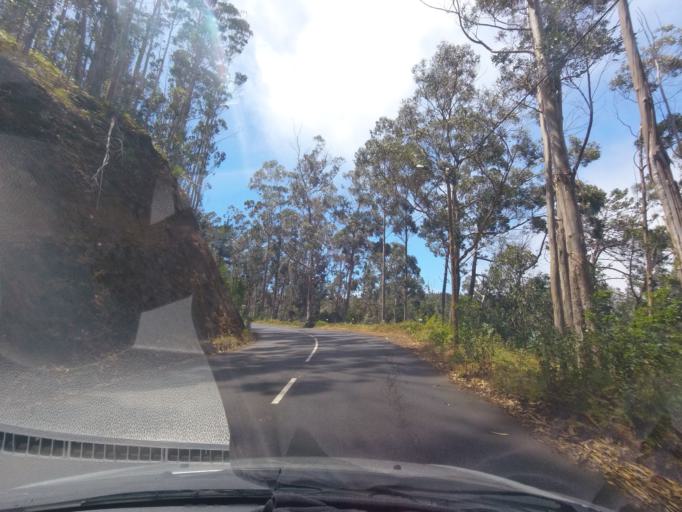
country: PT
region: Madeira
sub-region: Santa Cruz
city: Camacha
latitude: 32.6891
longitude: -16.8305
